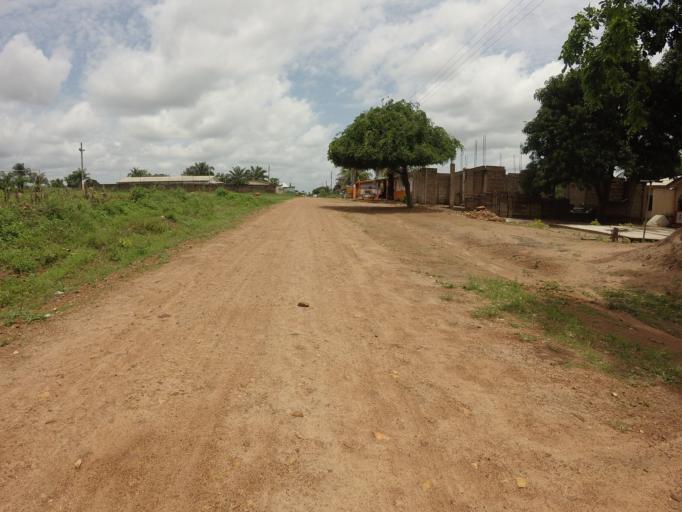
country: GH
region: Volta
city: Ho
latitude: 6.5778
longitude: 0.4603
